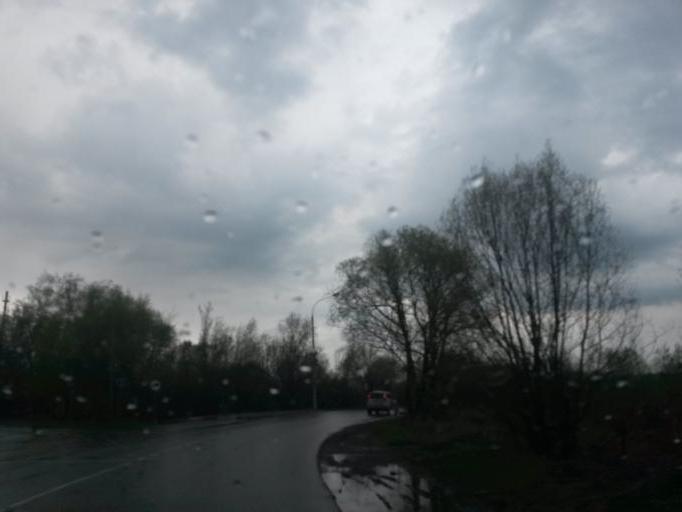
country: RU
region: Moskovskaya
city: Shcherbinka
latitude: 55.5075
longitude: 37.5933
